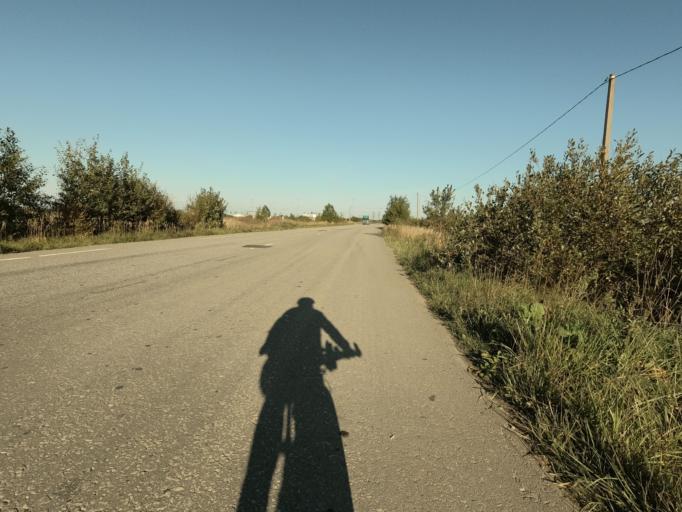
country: RU
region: St.-Petersburg
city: Petro-Slavyanka
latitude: 59.7698
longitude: 30.4957
